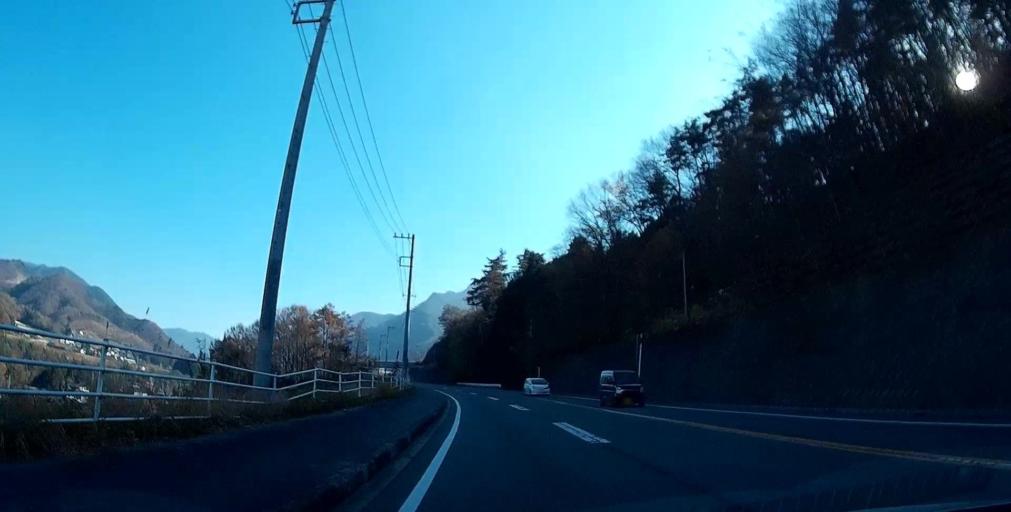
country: JP
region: Yamanashi
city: Isawa
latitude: 35.5998
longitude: 138.7087
